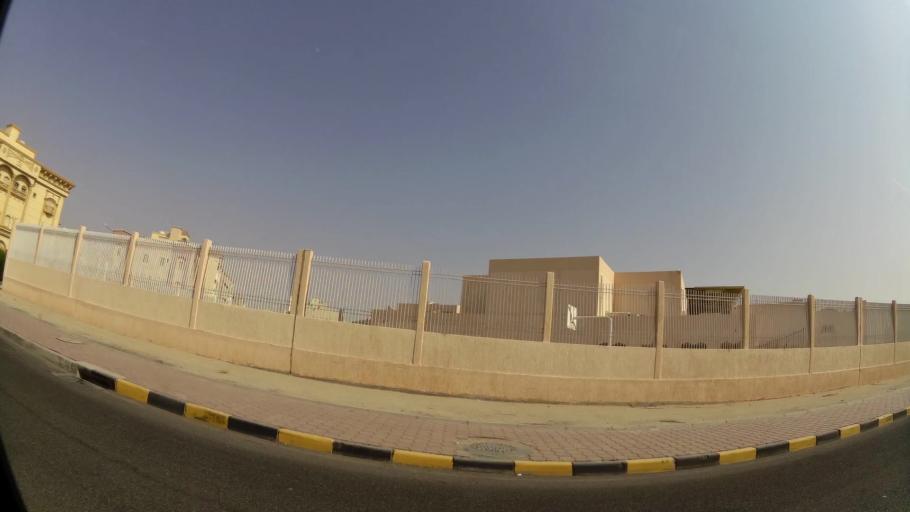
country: KW
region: Muhafazat al Jahra'
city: Al Jahra'
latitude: 29.3366
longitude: 47.7629
